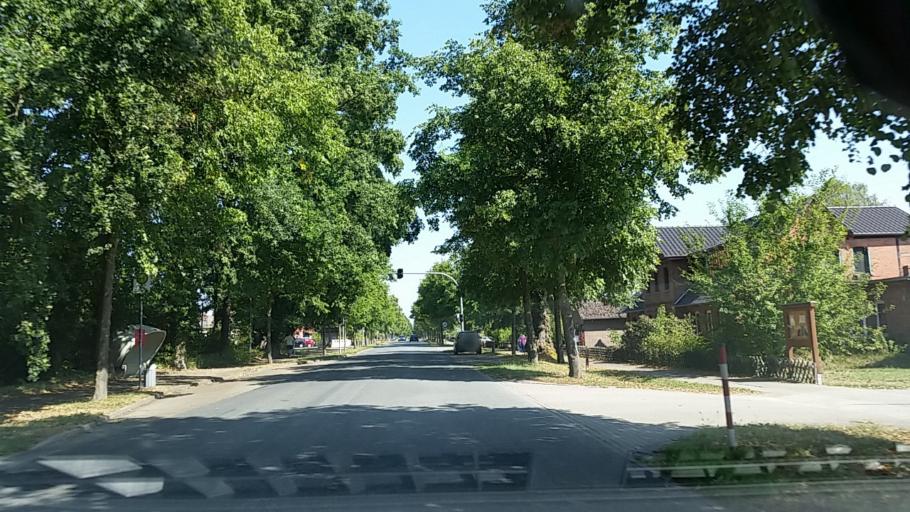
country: DE
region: Lower Saxony
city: Uelzen
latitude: 52.9261
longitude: 10.5279
